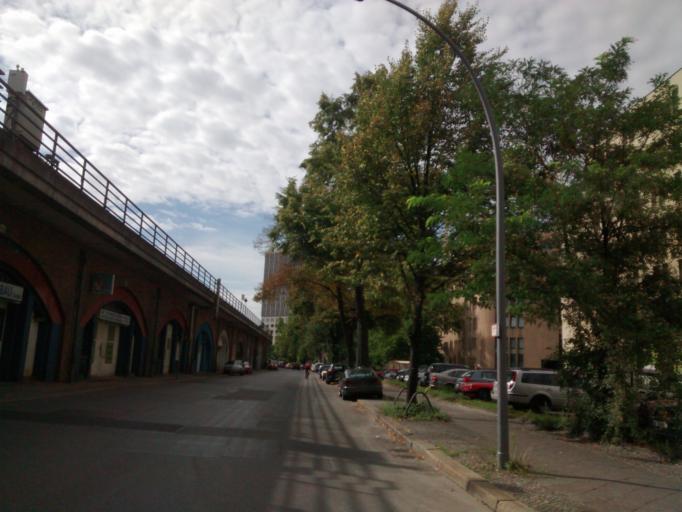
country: DE
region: Berlin
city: Hansaviertel
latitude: 52.5167
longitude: 13.3381
